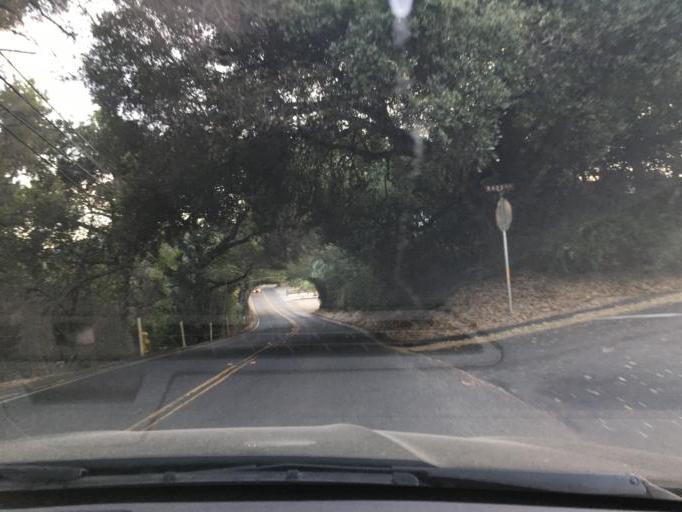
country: US
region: California
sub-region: Santa Clara County
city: Monte Sereno
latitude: 37.2487
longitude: -121.9964
